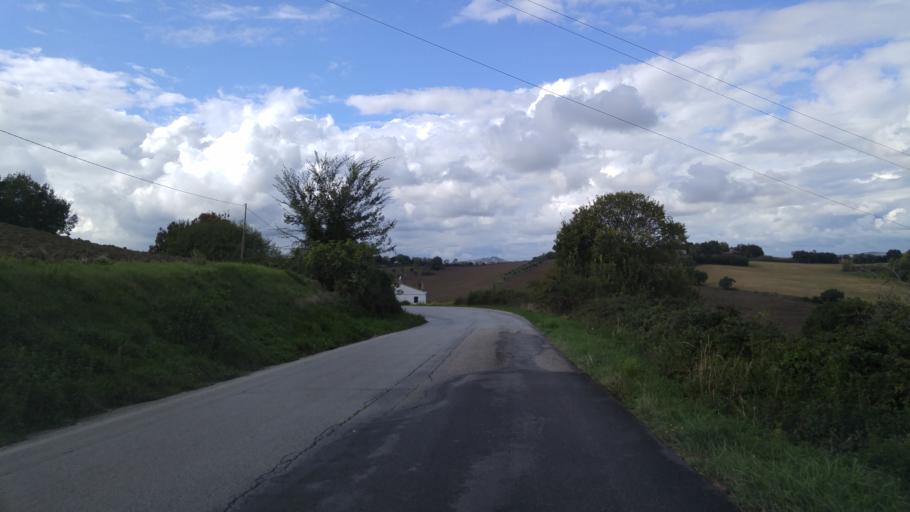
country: IT
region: The Marches
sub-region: Provincia di Pesaro e Urbino
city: Villa Ceccolini
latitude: 43.8580
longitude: 12.8749
